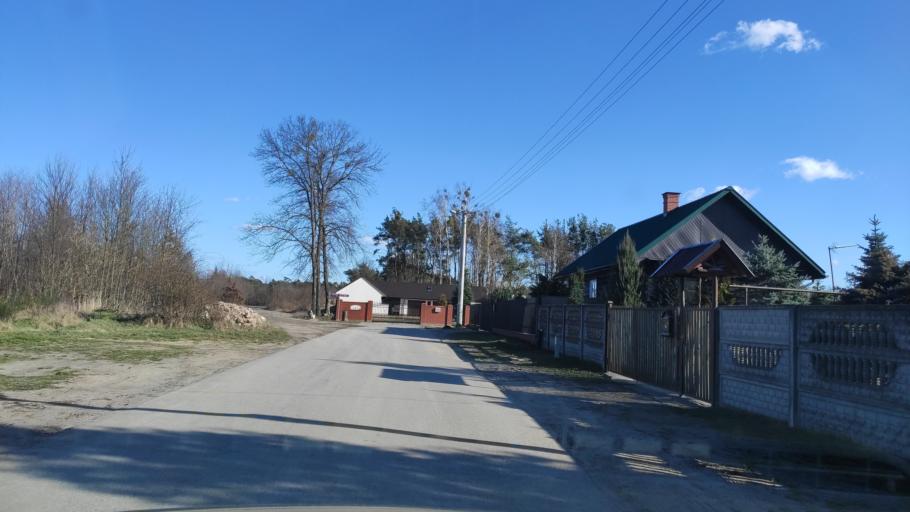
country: PL
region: Masovian Voivodeship
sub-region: Powiat radomski
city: Jastrzebia
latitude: 51.4557
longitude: 21.2719
